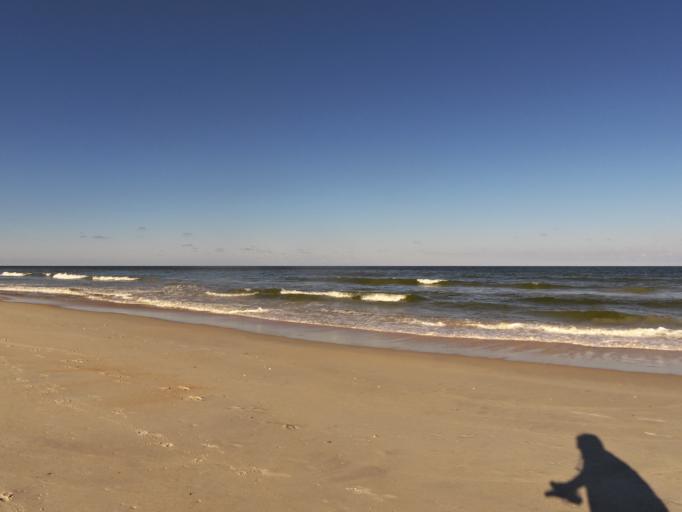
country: US
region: Florida
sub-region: Saint Johns County
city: Sawgrass
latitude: 30.1872
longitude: -81.3622
